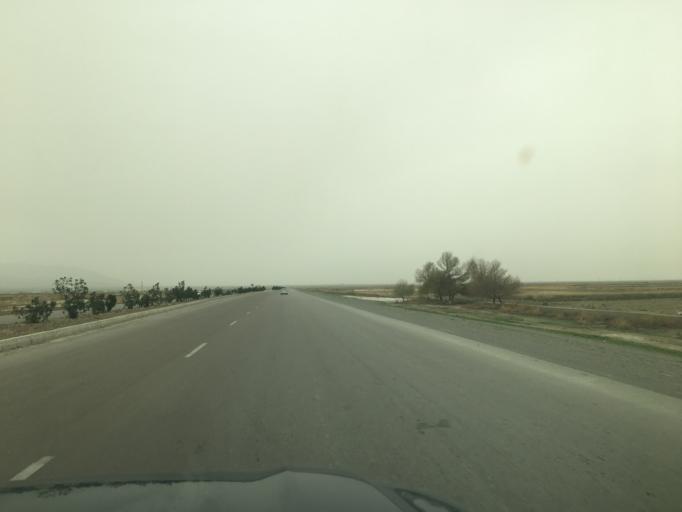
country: TM
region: Ahal
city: Baharly
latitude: 38.3590
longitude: 57.5354
